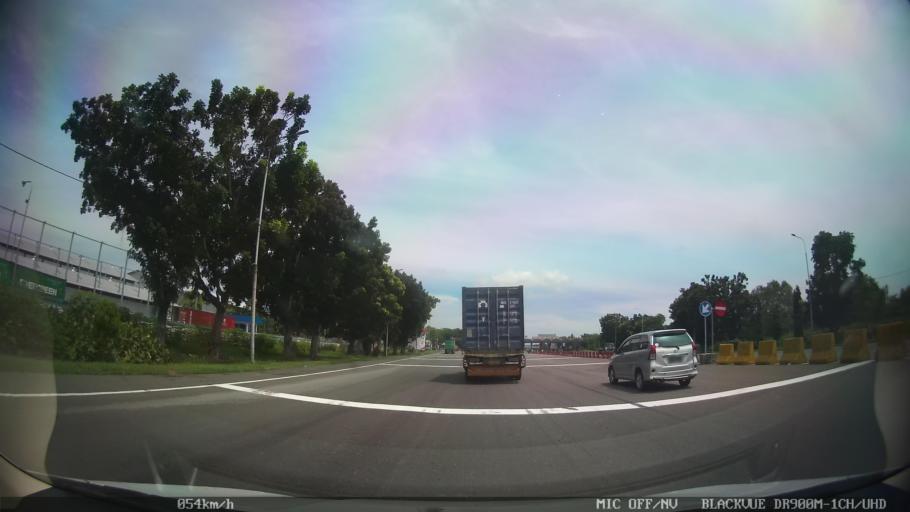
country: ID
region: North Sumatra
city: Labuhan Deli
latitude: 3.7268
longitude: 98.6817
